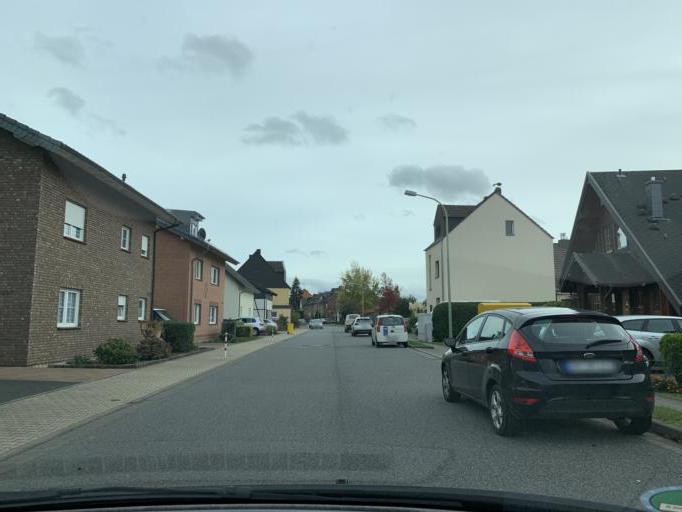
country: DE
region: North Rhine-Westphalia
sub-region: Regierungsbezirk Koln
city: Kreuzau
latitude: 50.7349
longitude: 6.5081
